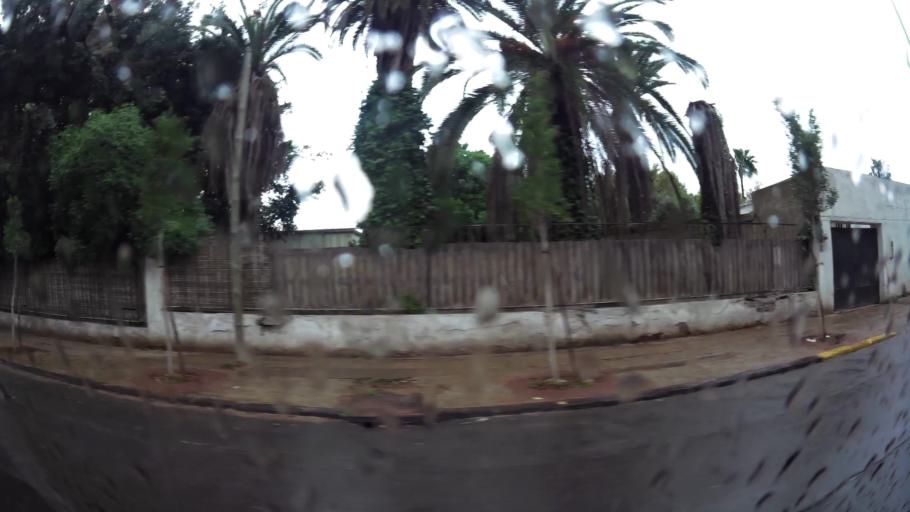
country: MA
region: Grand Casablanca
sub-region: Casablanca
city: Casablanca
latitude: 33.5774
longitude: -7.6178
